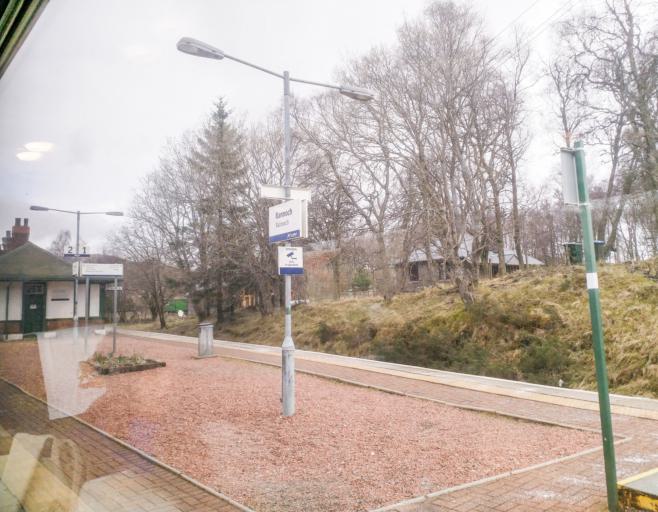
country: GB
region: Scotland
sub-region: Highland
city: Spean Bridge
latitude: 56.6856
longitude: -4.5772
